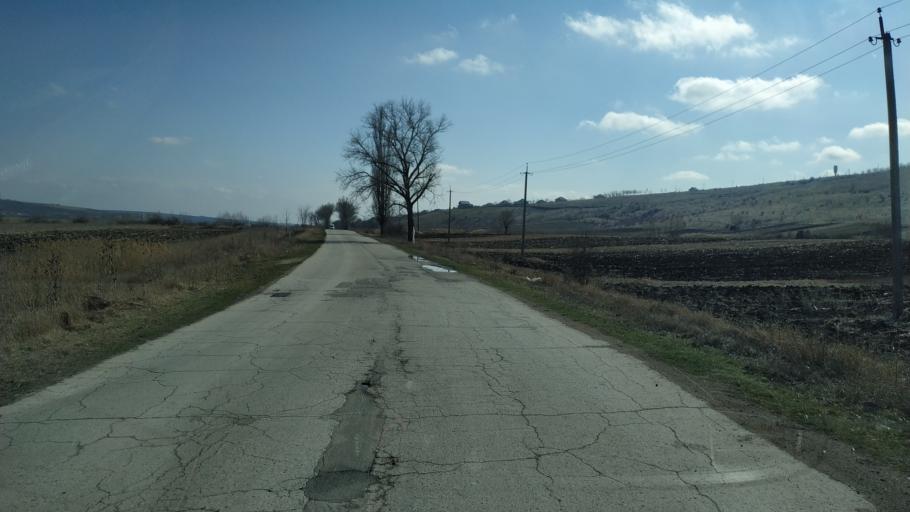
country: MD
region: Hincesti
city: Hincesti
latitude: 46.9419
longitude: 28.6254
